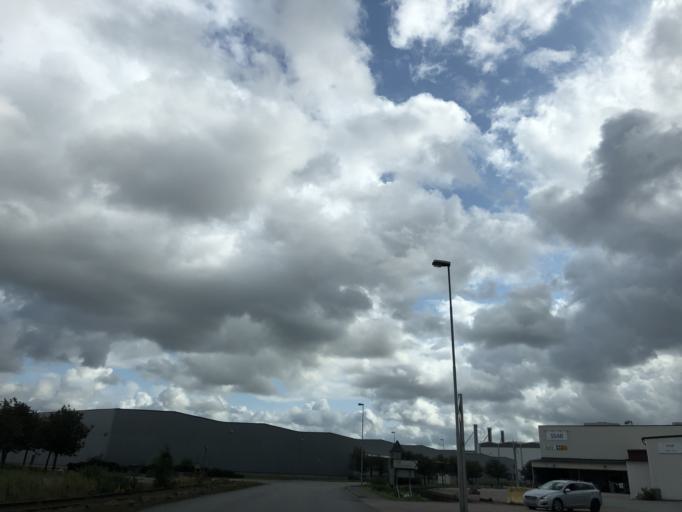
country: SE
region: Vaestra Goetaland
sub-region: Goteborg
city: Torslanda
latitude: 57.7020
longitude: 11.8199
